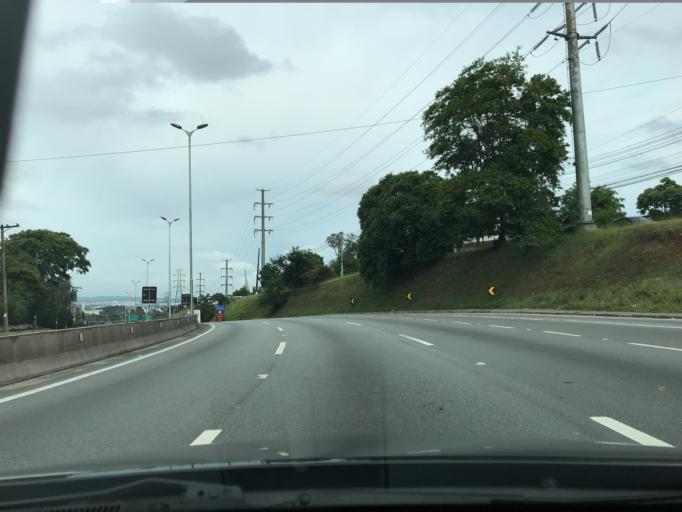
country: BR
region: Sao Paulo
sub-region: Embu
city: Embu
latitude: -23.5991
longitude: -46.8483
